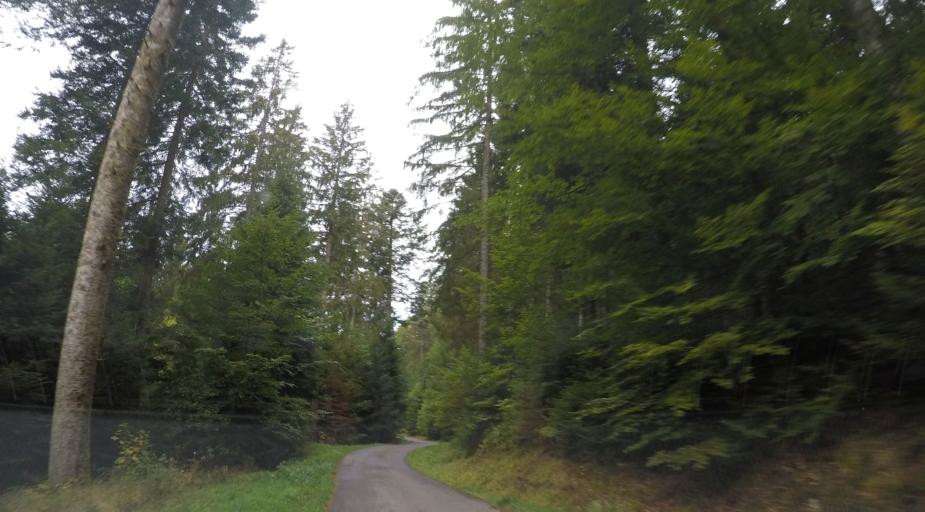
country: DE
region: Baden-Wuerttemberg
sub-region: Karlsruhe Region
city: Baiersbronn
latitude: 48.5022
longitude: 8.3211
